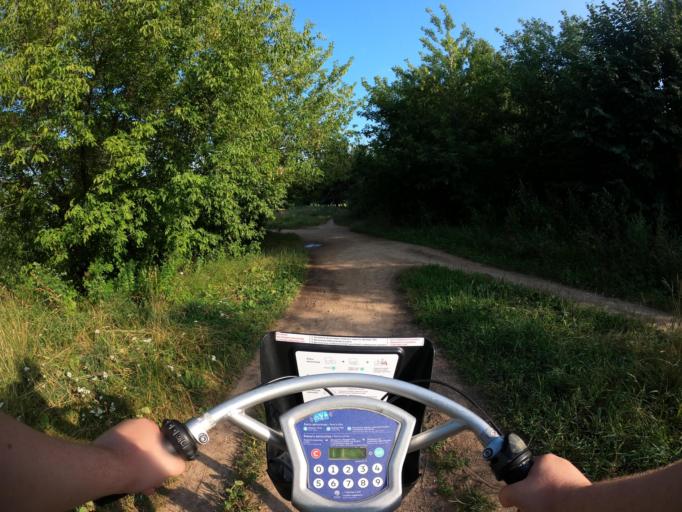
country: RU
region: Moscow
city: Strogino
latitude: 55.8153
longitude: 37.4114
